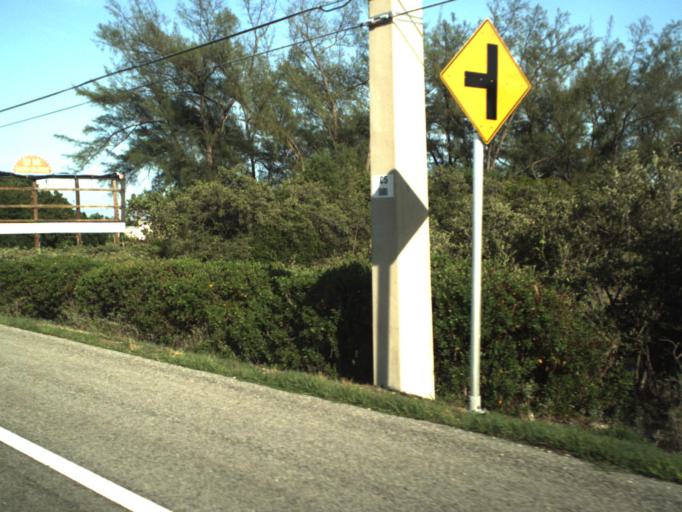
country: US
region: Florida
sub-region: Monroe County
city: Marathon
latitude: 24.7726
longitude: -80.9358
